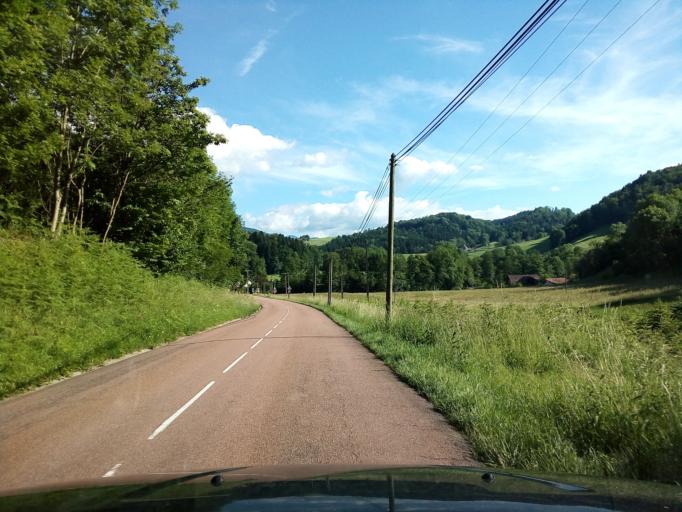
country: FR
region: Rhone-Alpes
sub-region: Departement de la Savoie
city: La Bridoire
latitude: 45.5269
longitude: 5.7626
